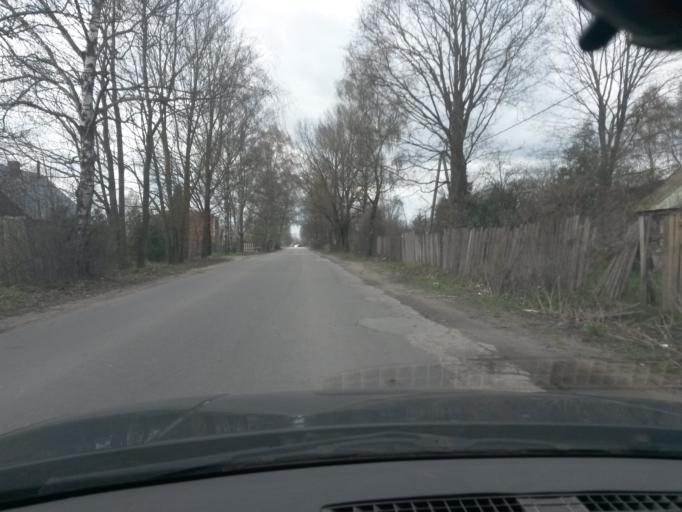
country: LV
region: Kekava
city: Kekava
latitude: 56.8967
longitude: 24.2336
